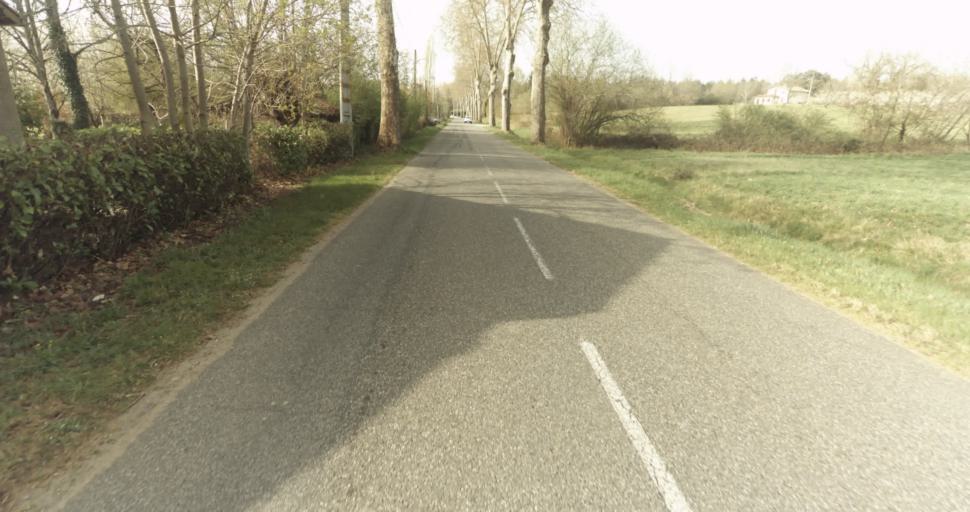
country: FR
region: Midi-Pyrenees
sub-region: Departement du Tarn-et-Garonne
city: Moissac
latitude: 44.1477
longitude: 1.1061
